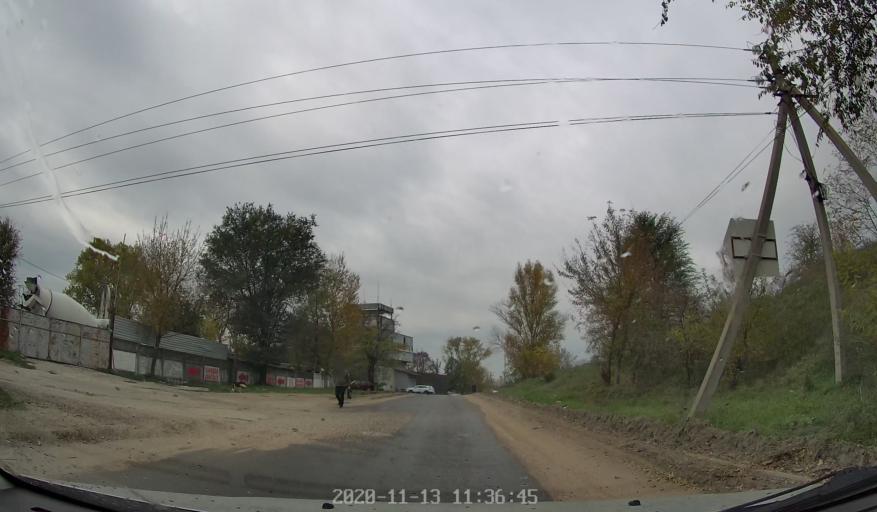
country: MD
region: Chisinau
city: Chisinau
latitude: 46.9893
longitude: 28.9160
